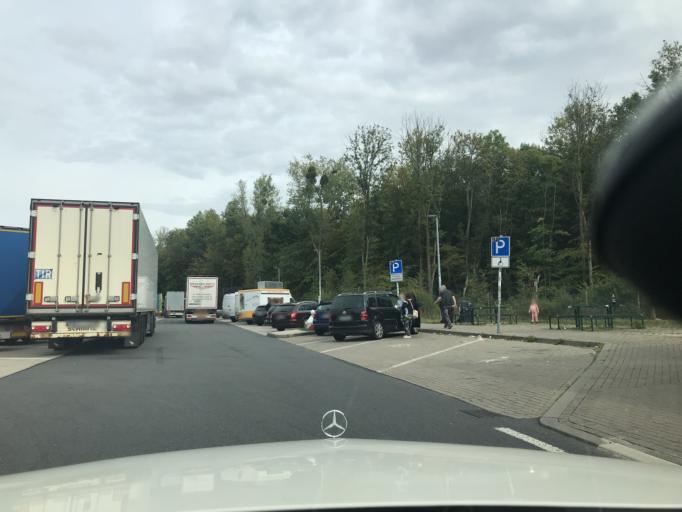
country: DE
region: North Rhine-Westphalia
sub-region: Regierungsbezirk Arnsberg
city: Bonen
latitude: 51.6061
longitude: 7.7343
